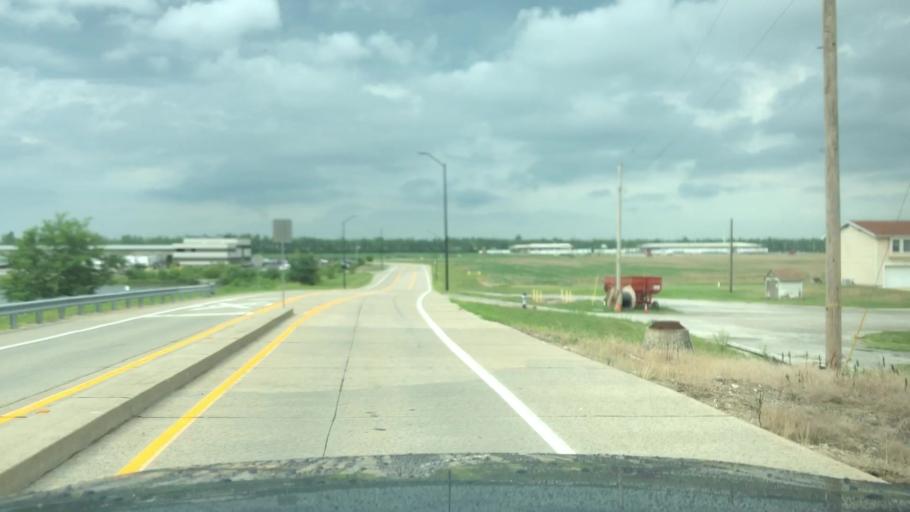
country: US
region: Missouri
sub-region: Saint Charles County
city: Saint Peters
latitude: 38.8043
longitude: -90.5808
